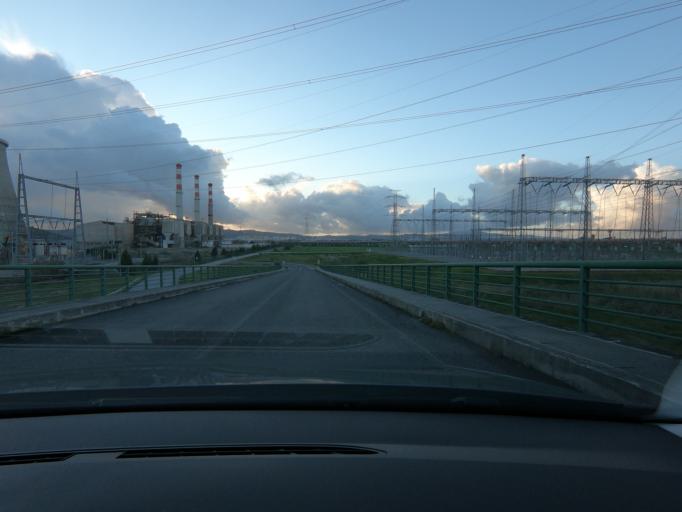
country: PT
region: Lisbon
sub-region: Alenquer
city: Carregado
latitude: 39.0123
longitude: -8.9501
